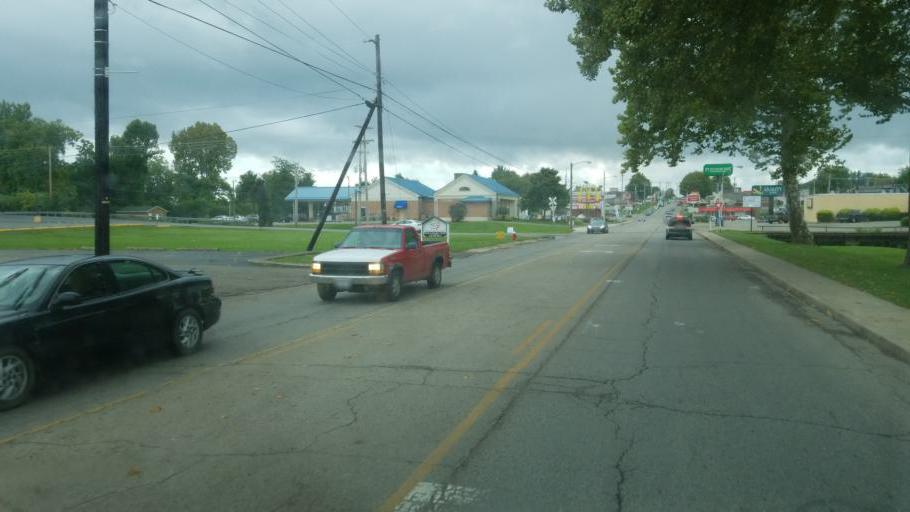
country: US
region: Ohio
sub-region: Jackson County
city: Jackson
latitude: 39.0467
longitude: -82.6313
